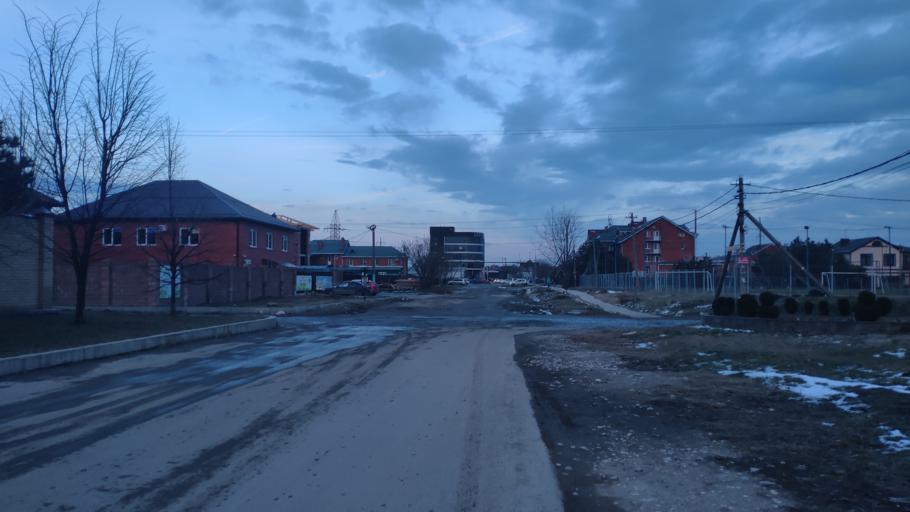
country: RU
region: Krasnodarskiy
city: Krasnodar
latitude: 45.0777
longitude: 39.0116
